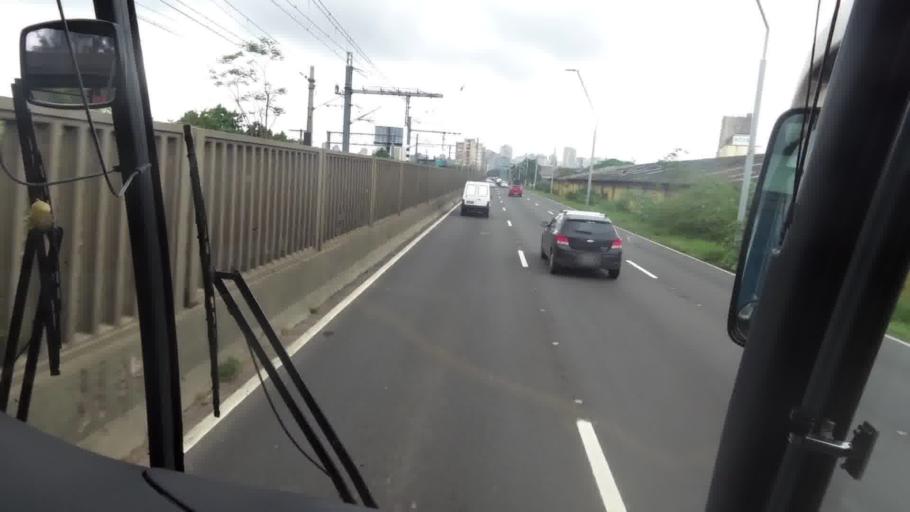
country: BR
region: Rio Grande do Sul
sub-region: Porto Alegre
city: Porto Alegre
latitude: -30.0151
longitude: -51.2141
